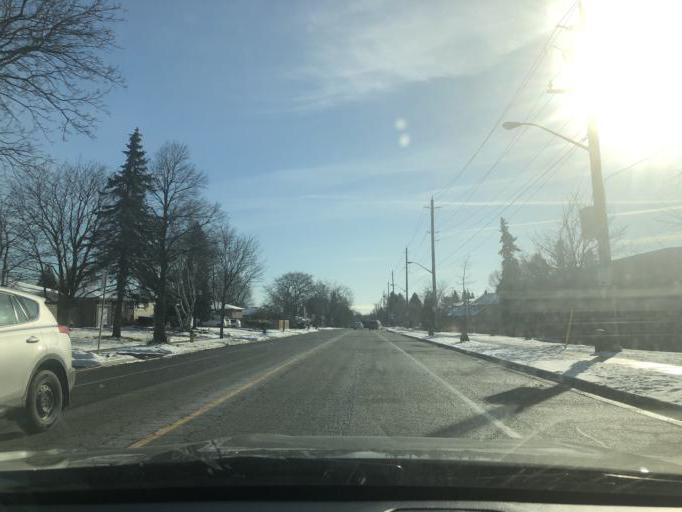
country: CA
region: Ontario
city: Scarborough
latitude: 43.7829
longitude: -79.1488
